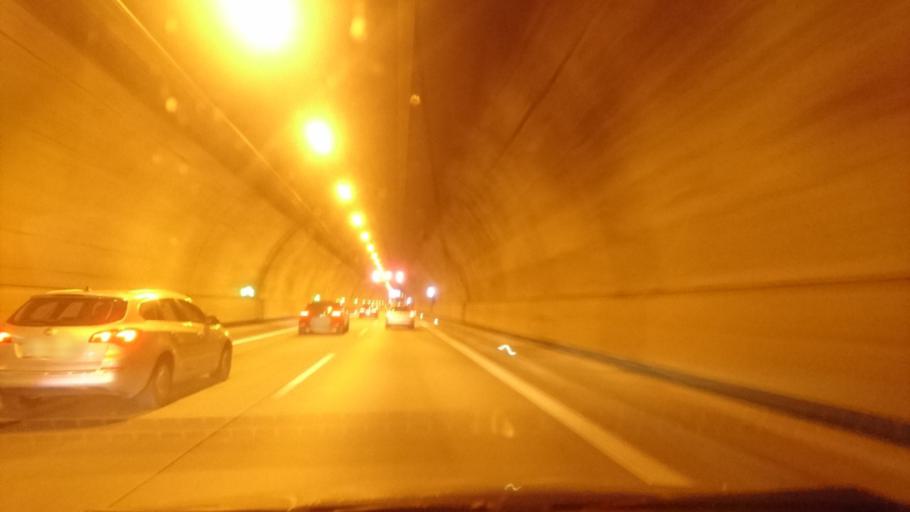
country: DE
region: Bavaria
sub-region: Upper Palatinate
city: Lappersdorf
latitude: 49.0329
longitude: 12.0838
